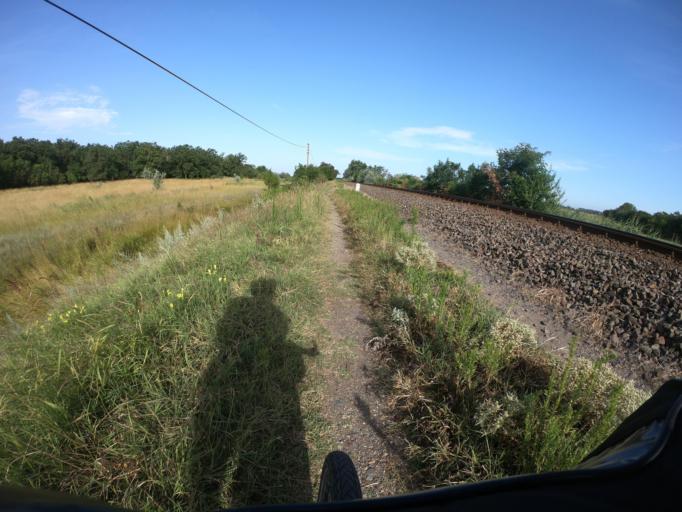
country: HU
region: Hajdu-Bihar
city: Tiszacsege
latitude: 47.6164
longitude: 21.0118
